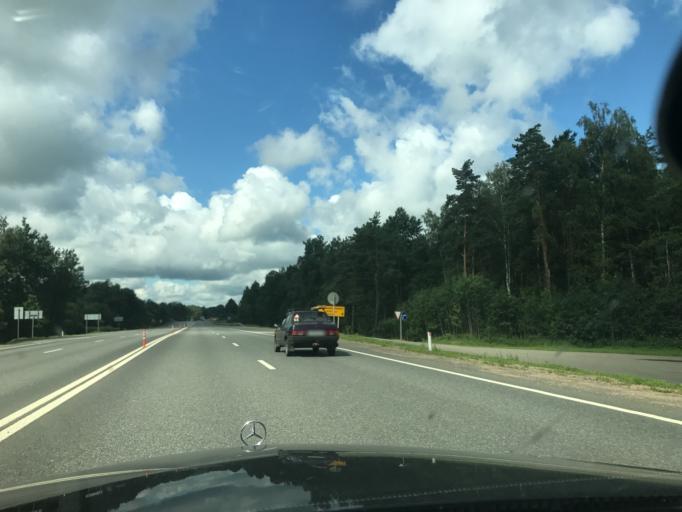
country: RU
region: Smolensk
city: Golynki
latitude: 54.7049
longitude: 31.2096
